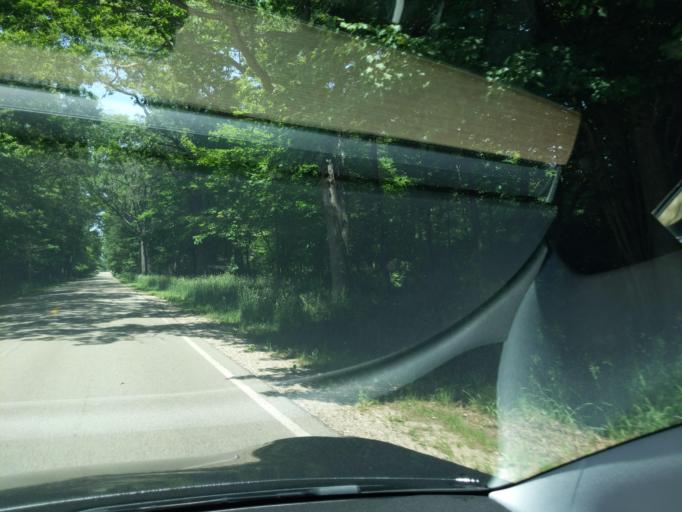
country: US
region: Michigan
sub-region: Muskegon County
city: Montague
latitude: 43.4073
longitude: -86.4165
